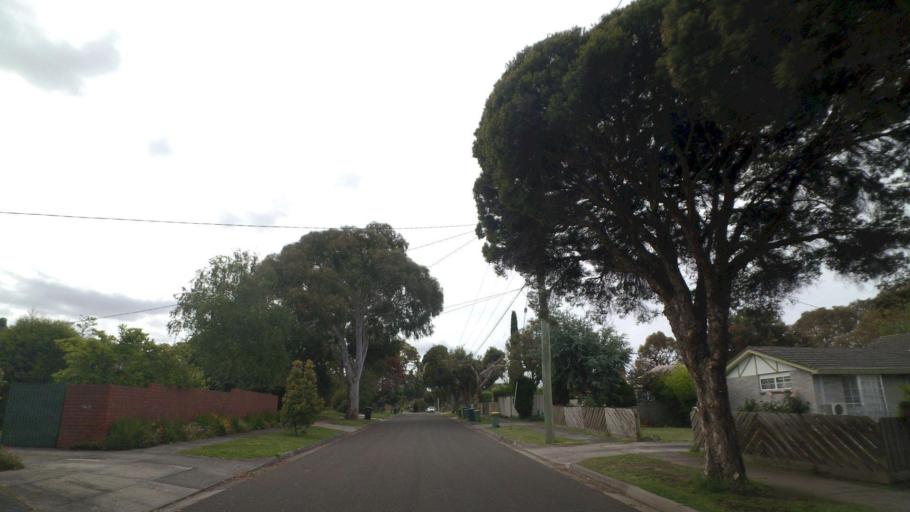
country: AU
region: Victoria
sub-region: Knox
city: Knoxfield
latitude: -37.8878
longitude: 145.2458
